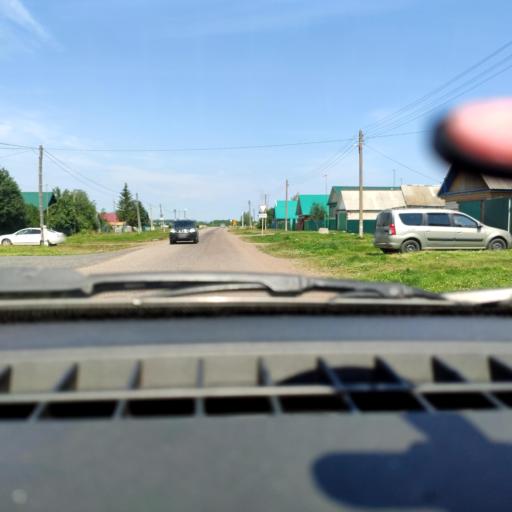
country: RU
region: Bashkortostan
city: Kabakovo
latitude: 54.4635
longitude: 55.9569
